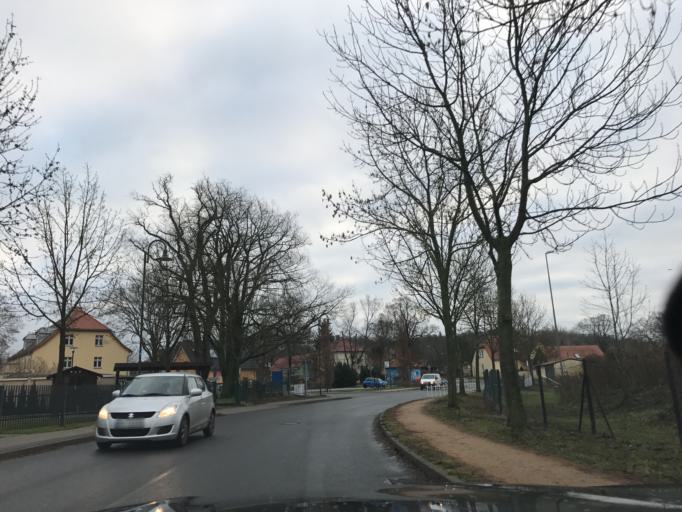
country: DE
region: Brandenburg
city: Werder
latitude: 52.3642
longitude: 12.9603
